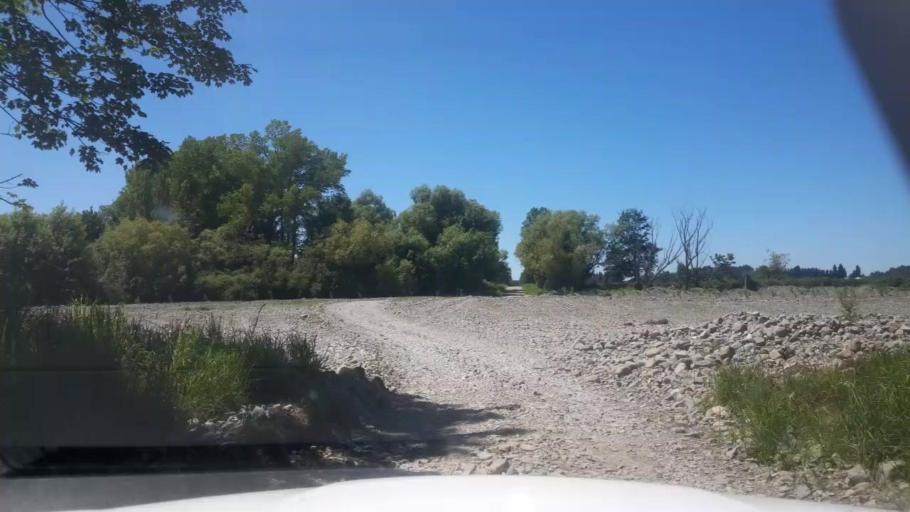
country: NZ
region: Canterbury
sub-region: Timaru District
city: Pleasant Point
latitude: -44.0470
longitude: 171.2349
